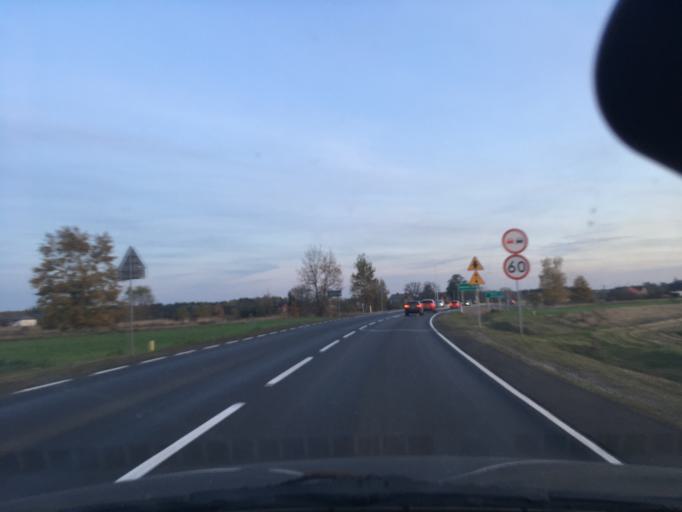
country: PL
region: Masovian Voivodeship
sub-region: Powiat plocki
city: Wyszogrod
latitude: 52.3589
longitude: 20.2064
